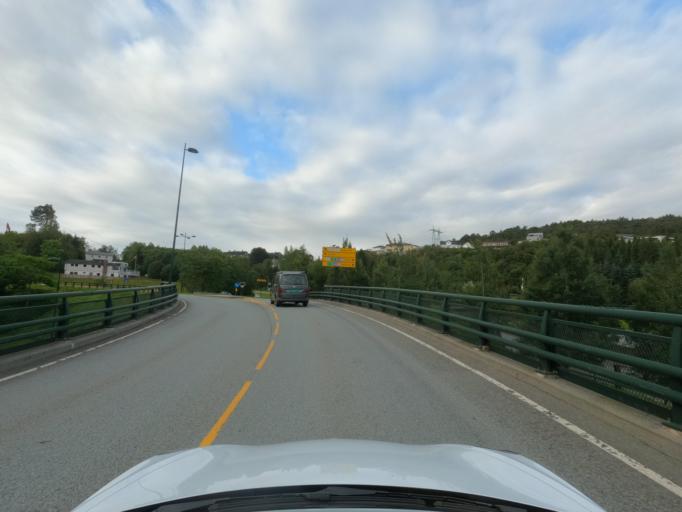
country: NO
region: Hordaland
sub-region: Bergen
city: Ytrebygda
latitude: 60.3099
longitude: 5.2680
